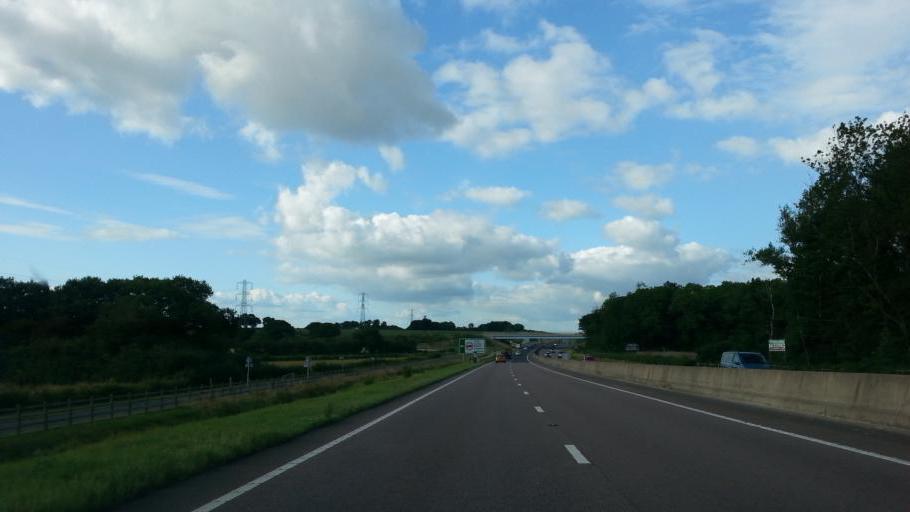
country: GB
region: England
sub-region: Nottinghamshire
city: Cotgrave
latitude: 52.8939
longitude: -1.0241
